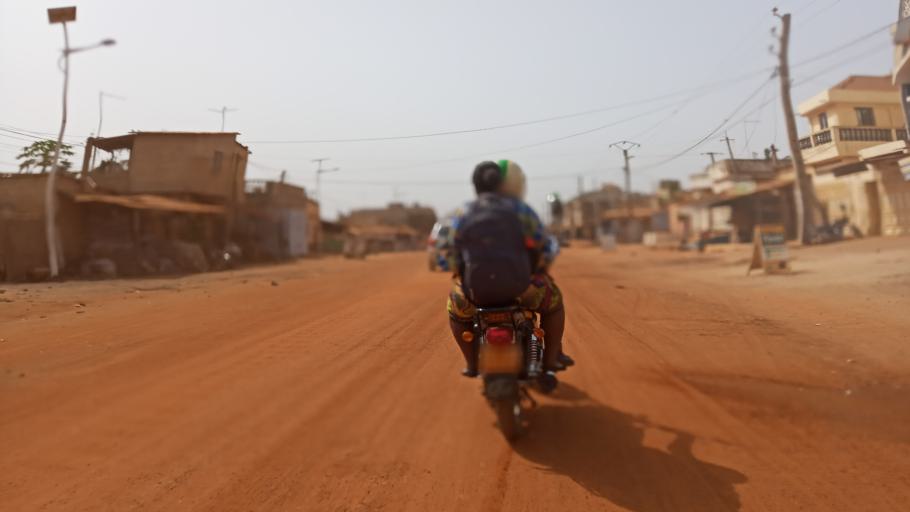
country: TG
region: Maritime
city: Lome
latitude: 6.1978
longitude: 1.1724
